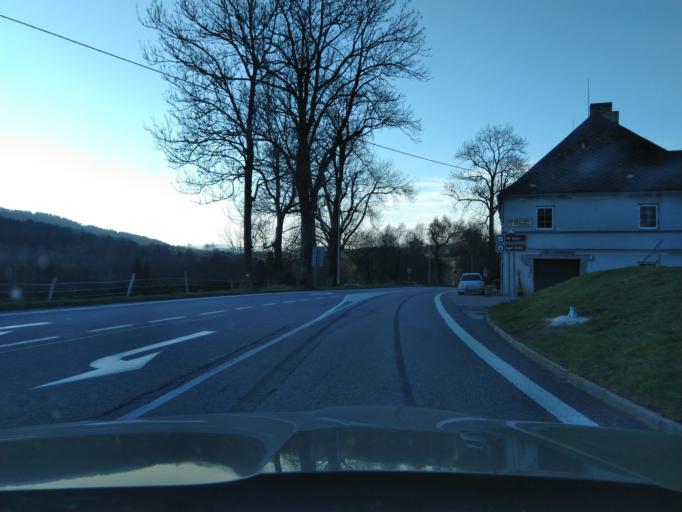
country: CZ
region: Jihocesky
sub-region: Okres Prachatice
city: Borova Lada
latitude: 48.9609
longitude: 13.7564
